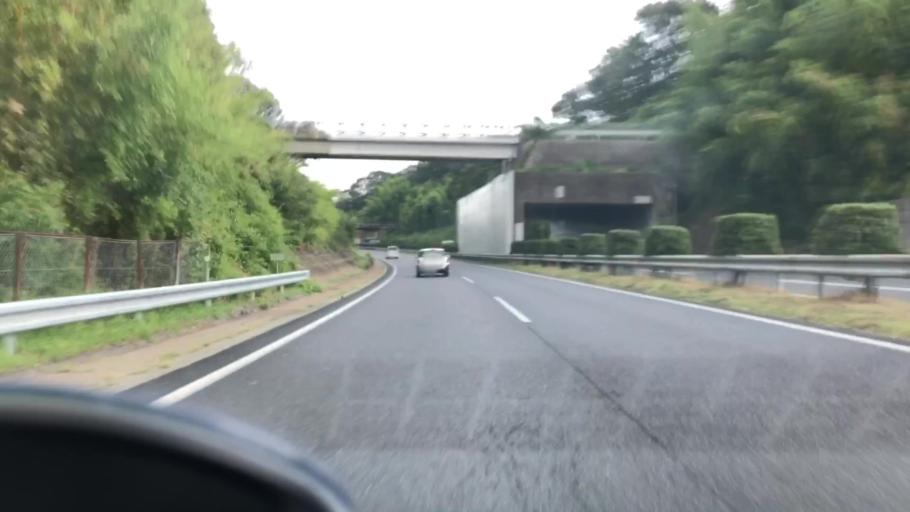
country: JP
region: Hyogo
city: Sandacho
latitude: 34.8863
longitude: 135.0992
